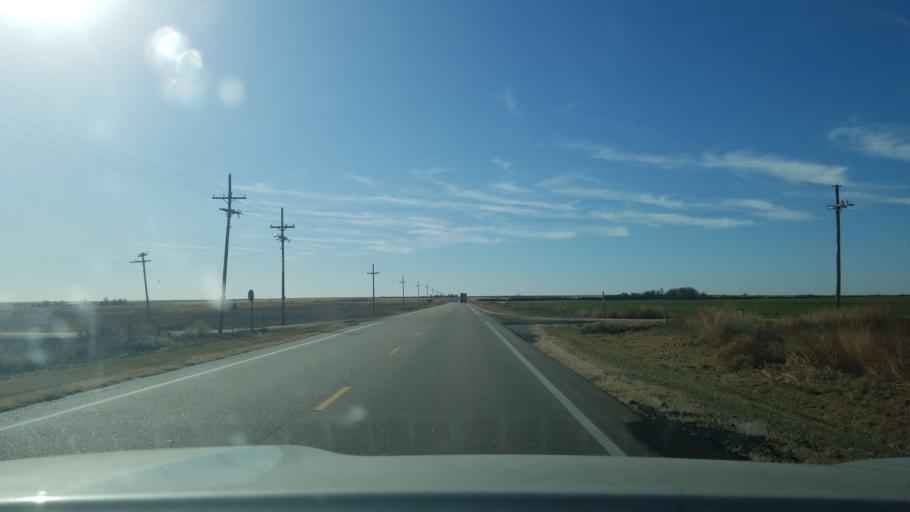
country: US
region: Kansas
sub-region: Ness County
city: Ness City
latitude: 38.4220
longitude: -99.8986
